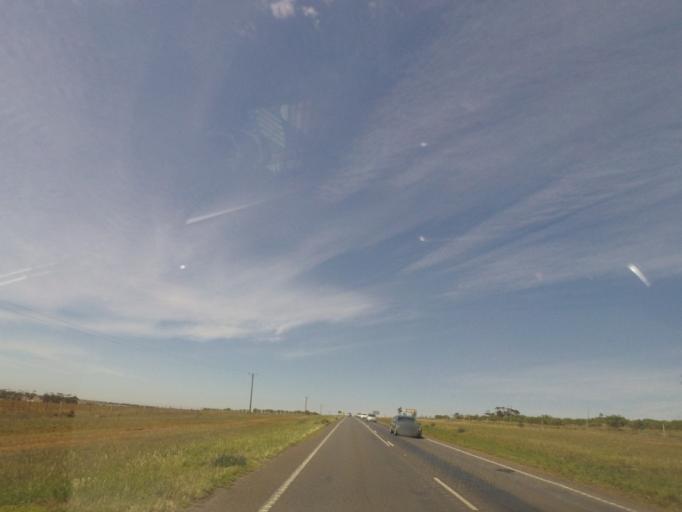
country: AU
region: Victoria
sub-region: Moorabool
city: Bacchus Marsh
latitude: -37.7707
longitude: 144.4391
